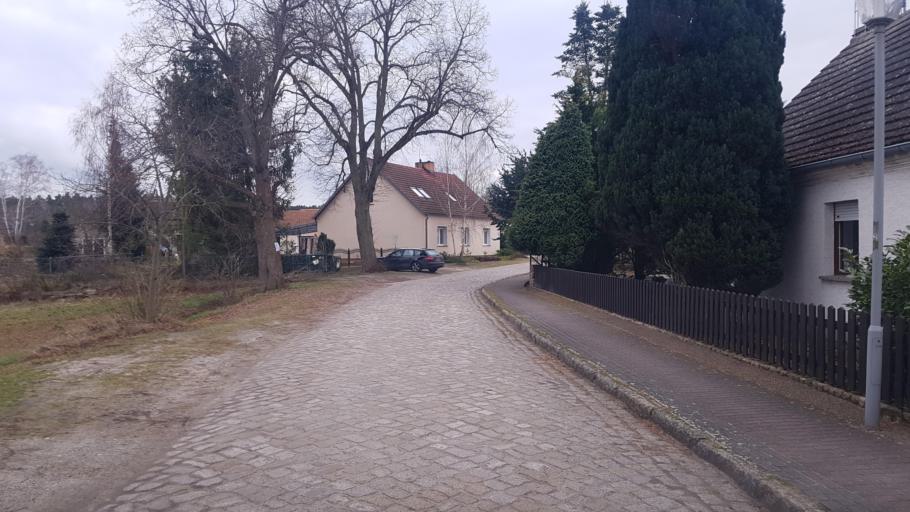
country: DE
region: Brandenburg
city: Halbe
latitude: 52.0668
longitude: 13.6920
